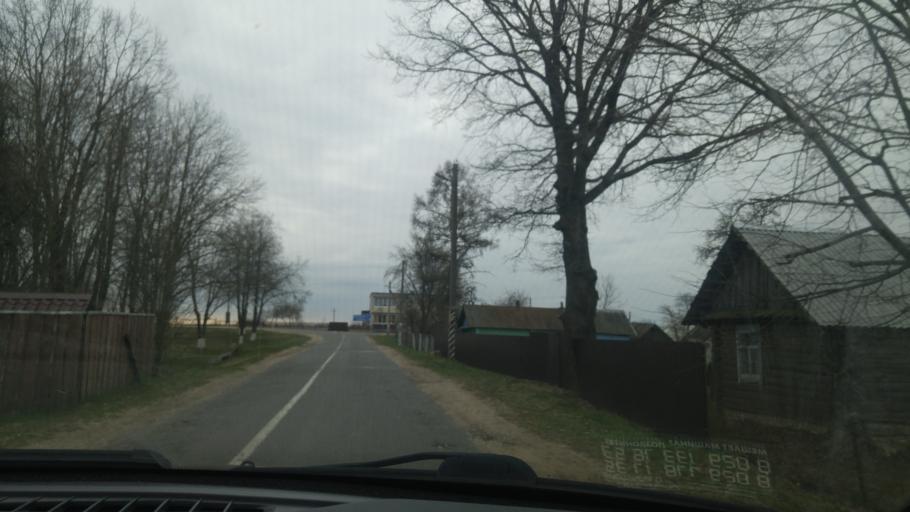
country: BY
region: Minsk
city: Blon'
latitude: 53.6748
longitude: 28.1845
